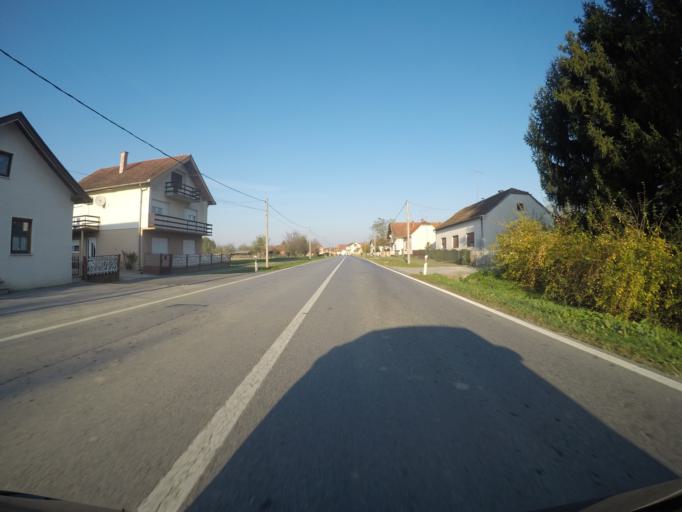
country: HU
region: Somogy
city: Barcs
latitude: 45.9007
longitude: 17.4378
